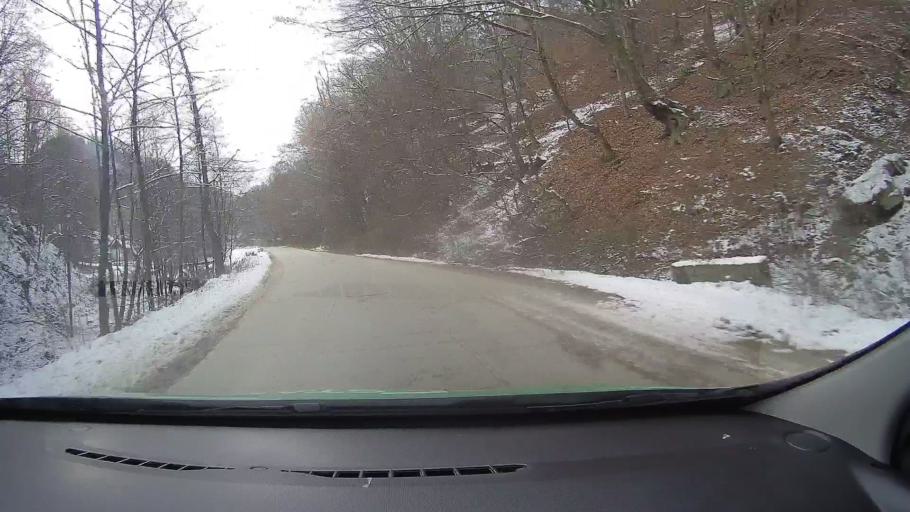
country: RO
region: Alba
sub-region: Oras Zlatna
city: Zlatna
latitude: 46.1097
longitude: 23.1973
